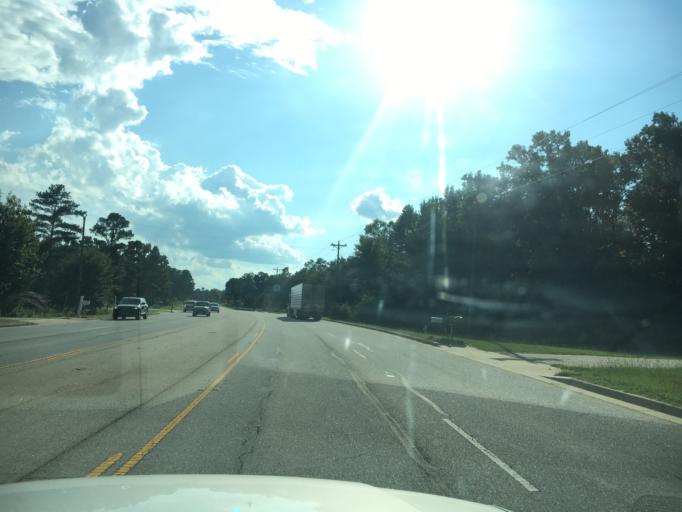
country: US
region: South Carolina
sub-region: Greenwood County
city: Ninety Six
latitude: 34.2900
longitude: -82.0381
